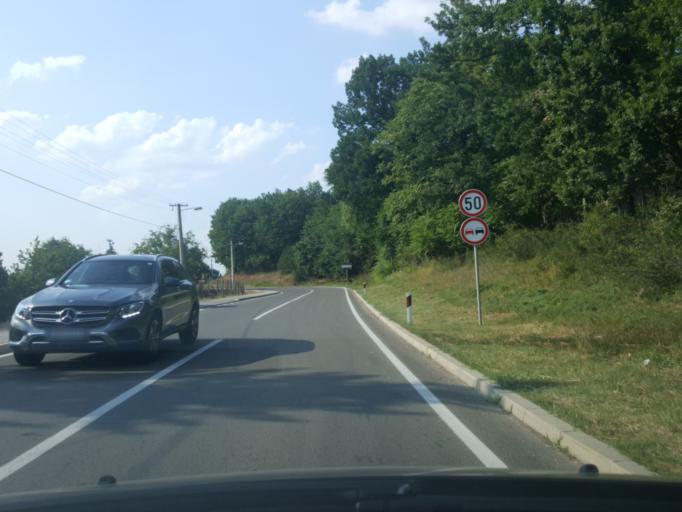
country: RS
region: Central Serbia
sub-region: Sumadijski Okrug
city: Topola
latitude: 44.2397
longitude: 20.6775
